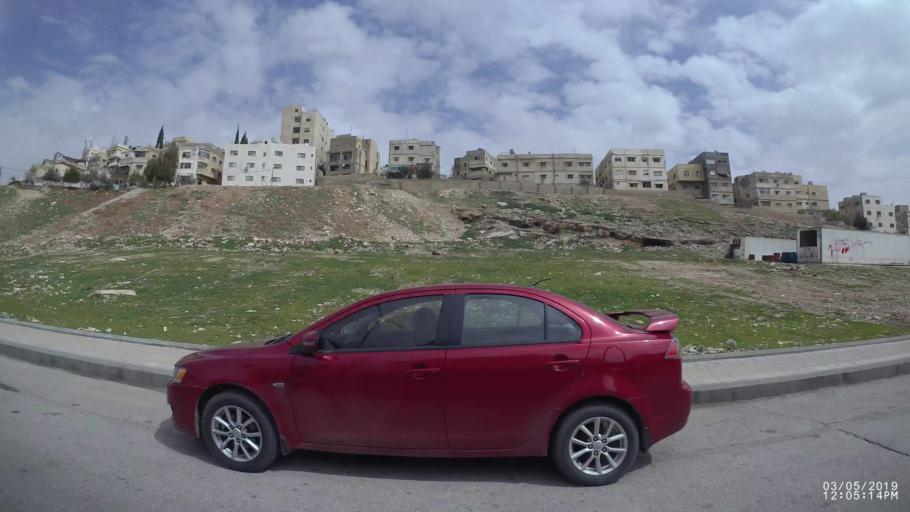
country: JO
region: Amman
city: Amman
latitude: 31.9770
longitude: 35.9191
